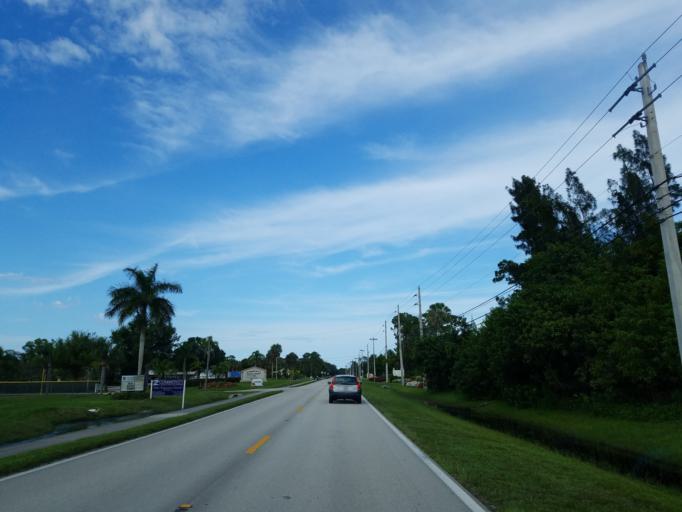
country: US
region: Florida
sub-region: Martin County
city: Palm City
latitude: 27.1272
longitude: -80.2443
